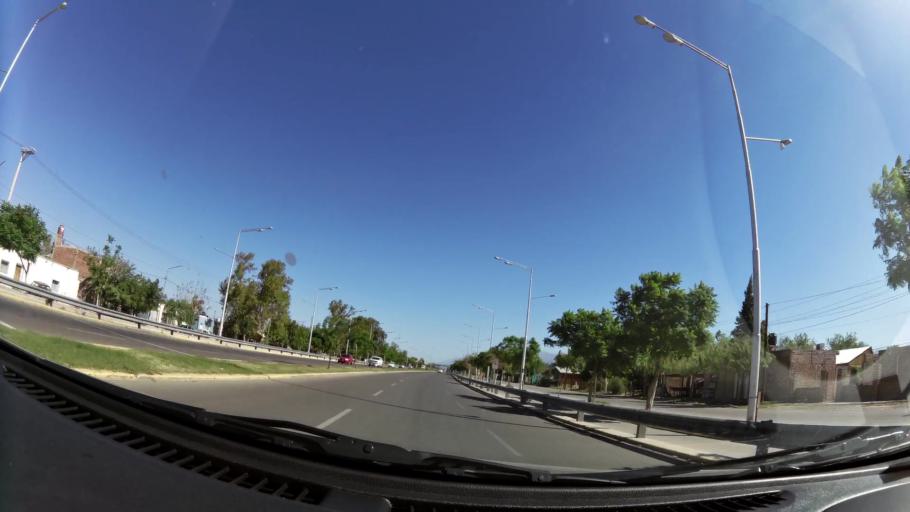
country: AR
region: San Juan
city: San Juan
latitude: -31.5485
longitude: -68.5369
